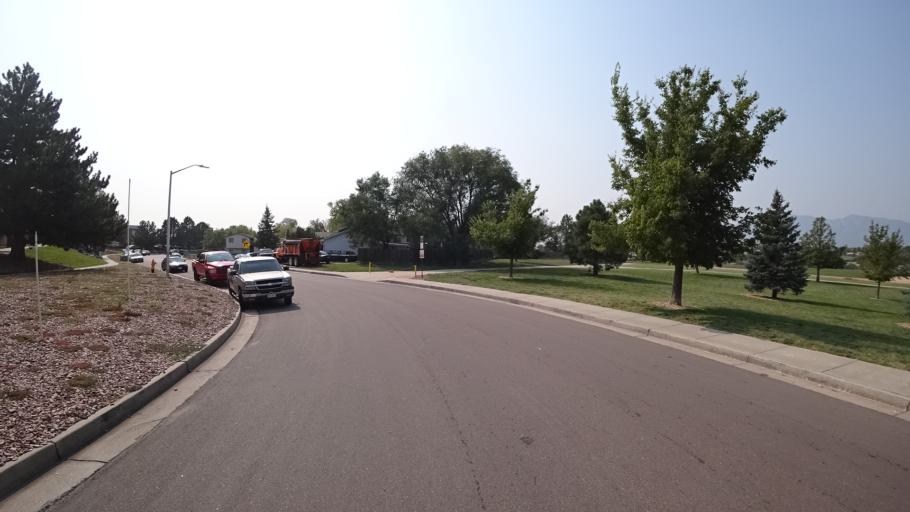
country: US
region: Colorado
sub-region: El Paso County
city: Stratmoor
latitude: 38.8122
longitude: -104.7622
